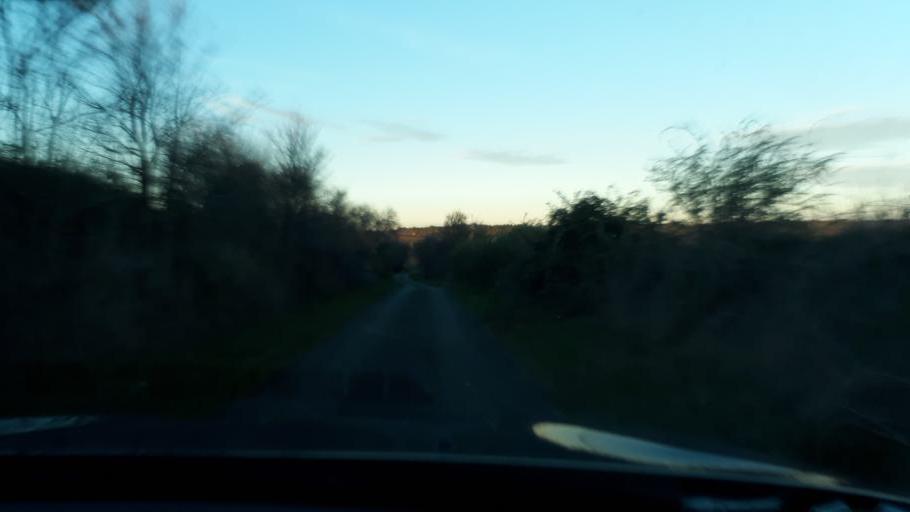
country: FR
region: Languedoc-Roussillon
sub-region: Departement de l'Herault
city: Florensac
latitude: 43.3992
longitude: 3.4594
